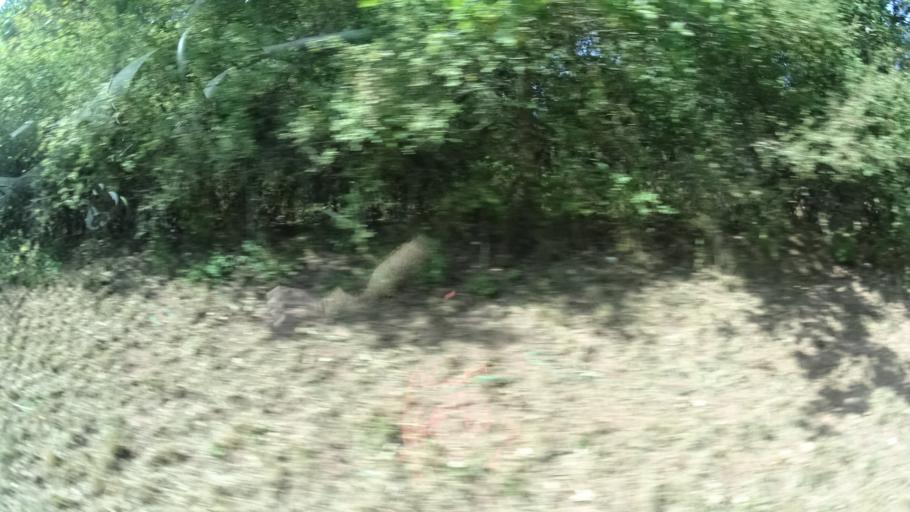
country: DE
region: Thuringia
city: Wallbach
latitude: 50.6352
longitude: 10.4064
